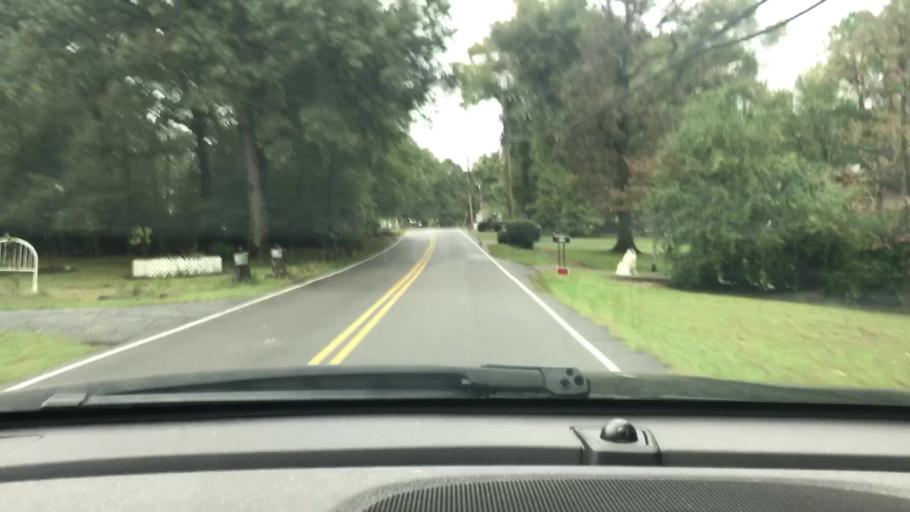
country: US
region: Tennessee
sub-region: Cheatham County
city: Kingston Springs
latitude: 36.1101
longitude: -87.1428
